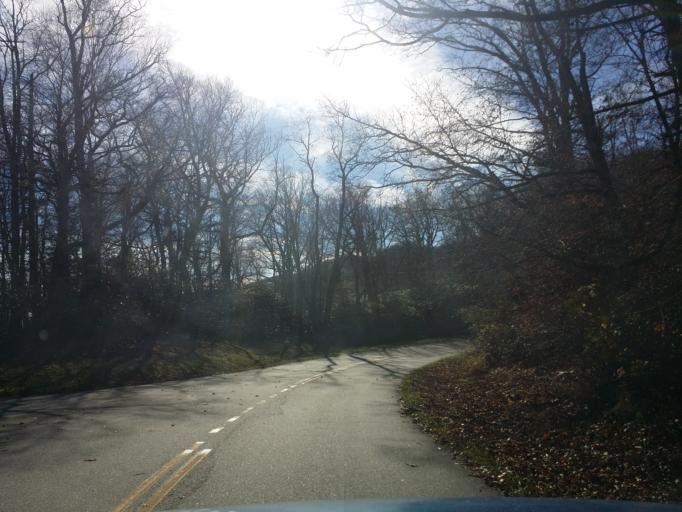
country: US
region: North Carolina
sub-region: McDowell County
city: West Marion
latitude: 35.7564
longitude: -82.1770
